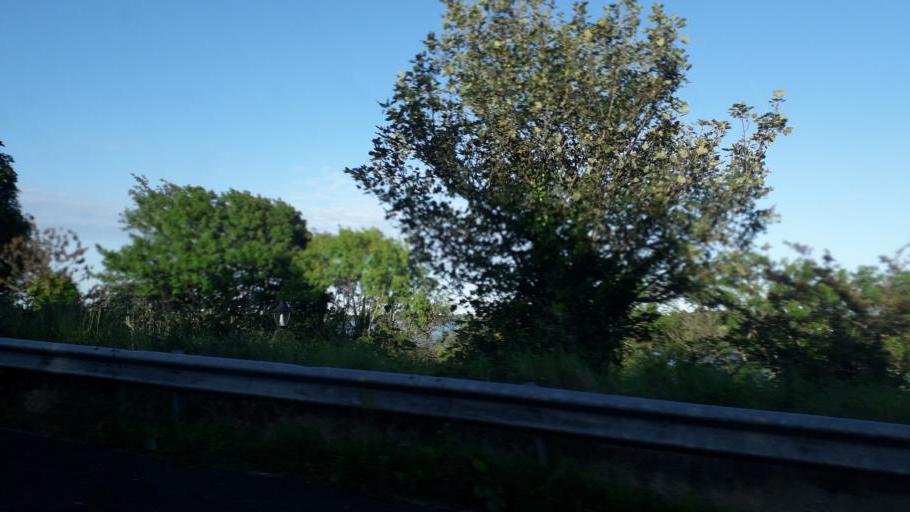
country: IE
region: Leinster
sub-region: Loch Garman
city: Loch Garman
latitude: 52.3541
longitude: -6.5071
